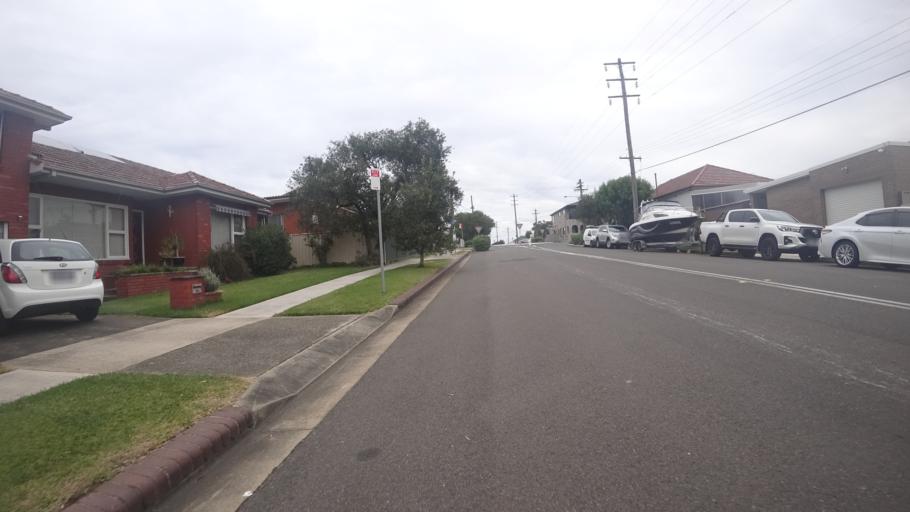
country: AU
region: New South Wales
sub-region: Rockdale
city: Bardwell Valley
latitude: -33.9411
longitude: 151.1287
